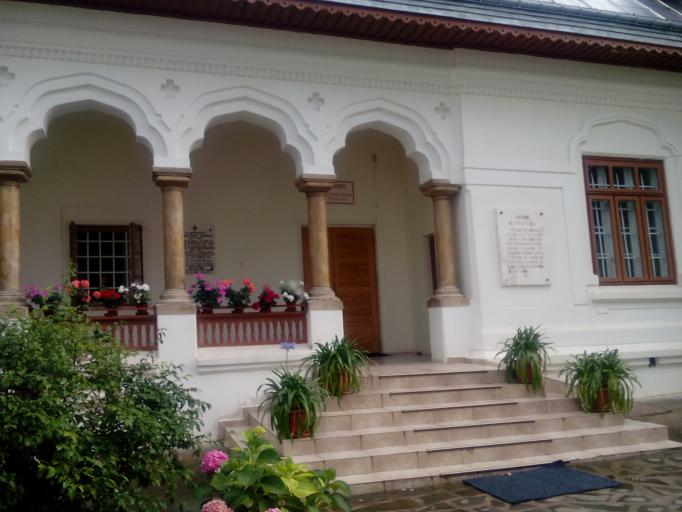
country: RO
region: Neamt
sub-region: Comuna Agapia
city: Filioara
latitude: 47.1396
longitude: 26.2683
